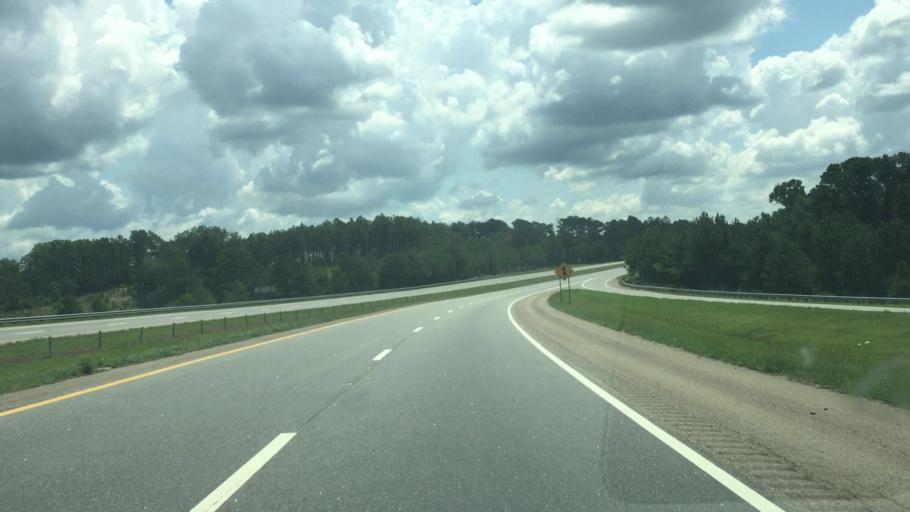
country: US
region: North Carolina
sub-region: Richmond County
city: Hamlet
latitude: 34.8685
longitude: -79.6453
